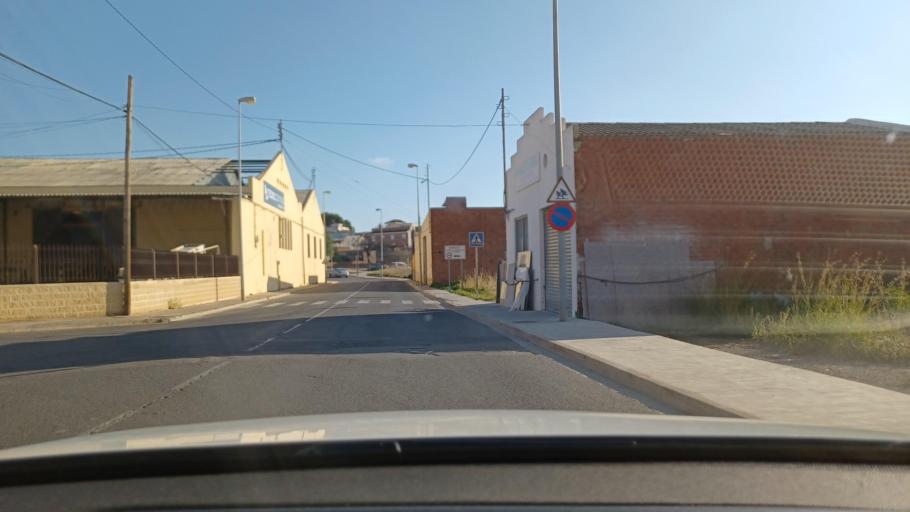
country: ES
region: Valencia
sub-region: Provincia de Castello
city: Onda
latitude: 39.9640
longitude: -0.2517
